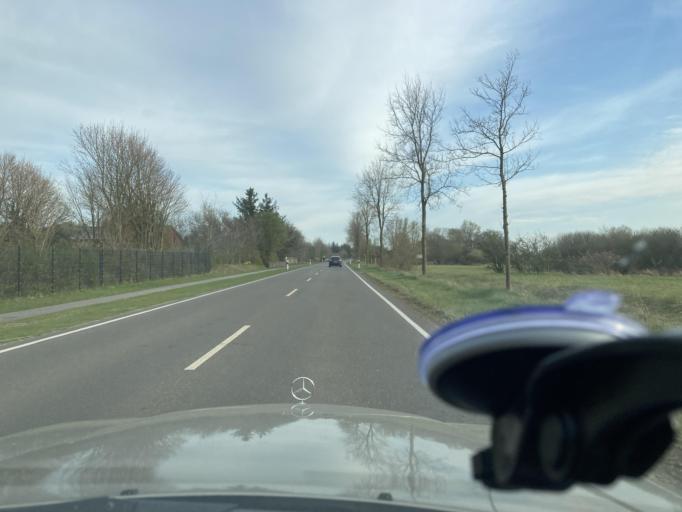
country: DE
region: Schleswig-Holstein
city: Stelle-Wittenwurth
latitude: 54.2909
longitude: 9.0420
